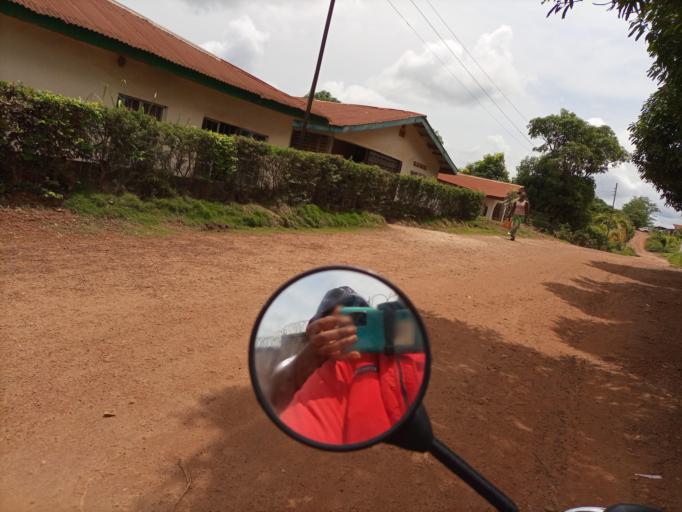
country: SL
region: Southern Province
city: Bo
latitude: 7.9710
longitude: -11.7212
